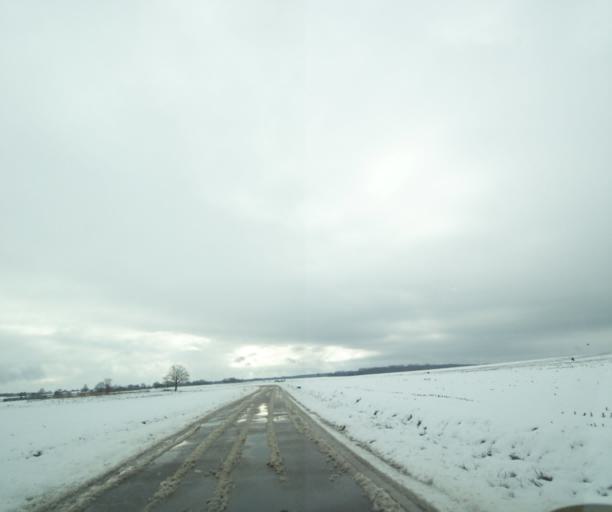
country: FR
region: Champagne-Ardenne
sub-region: Departement de la Haute-Marne
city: Montier-en-Der
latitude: 48.4441
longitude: 4.7054
